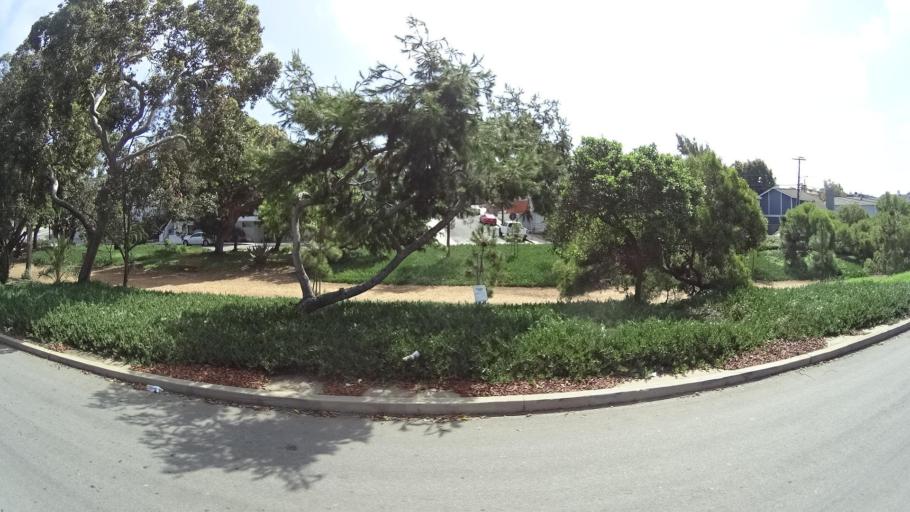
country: US
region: California
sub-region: Los Angeles County
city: Hermosa Beach
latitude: 33.8598
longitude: -118.3942
